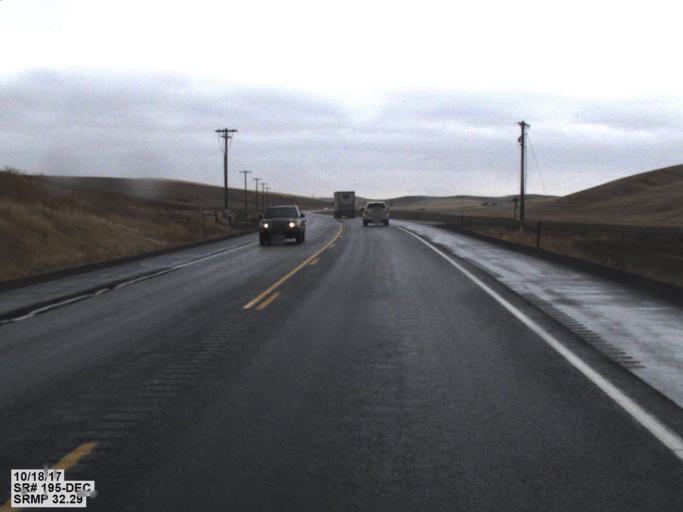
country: US
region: Washington
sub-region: Whitman County
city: Colfax
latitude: 46.8147
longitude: -117.3217
